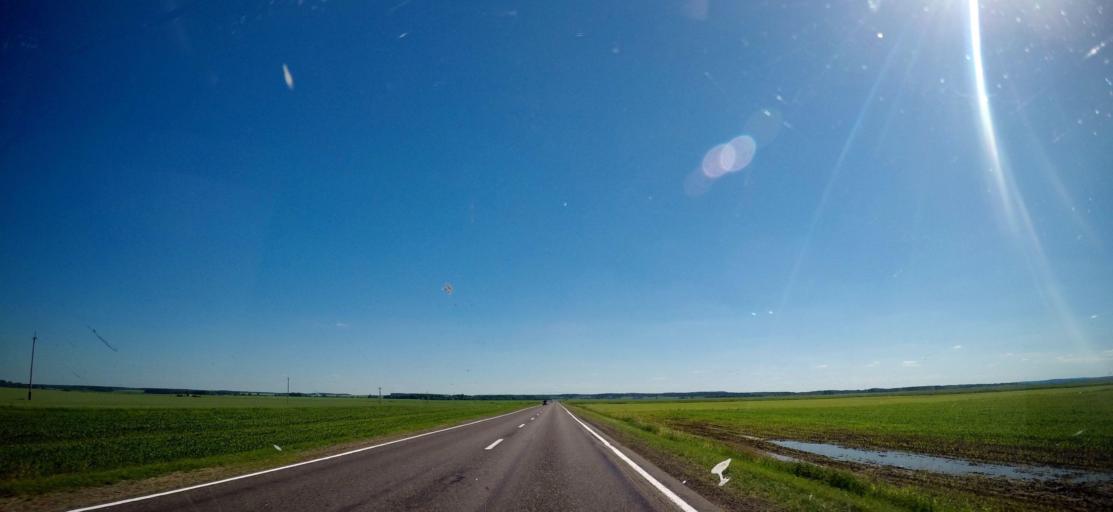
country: BY
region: Grodnenskaya
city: Indura
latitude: 53.3721
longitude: 23.9486
